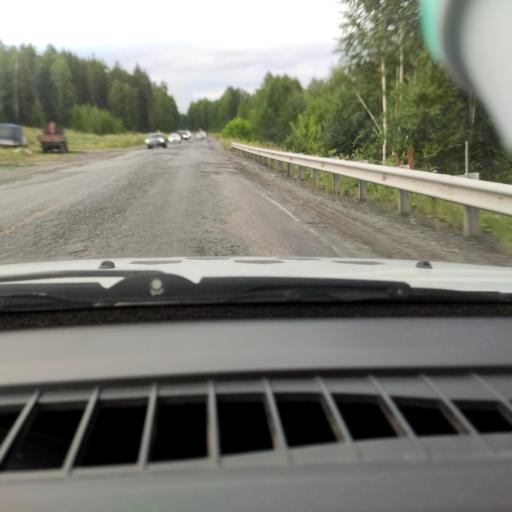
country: RU
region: Chelyabinsk
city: Karabash
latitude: 55.5270
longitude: 60.3379
